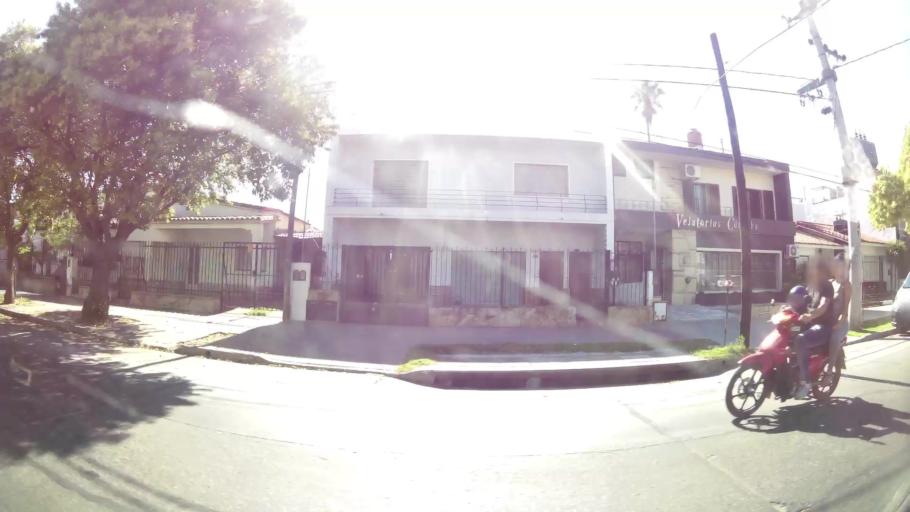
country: AR
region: Cordoba
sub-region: Departamento de Capital
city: Cordoba
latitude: -31.4369
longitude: -64.1688
